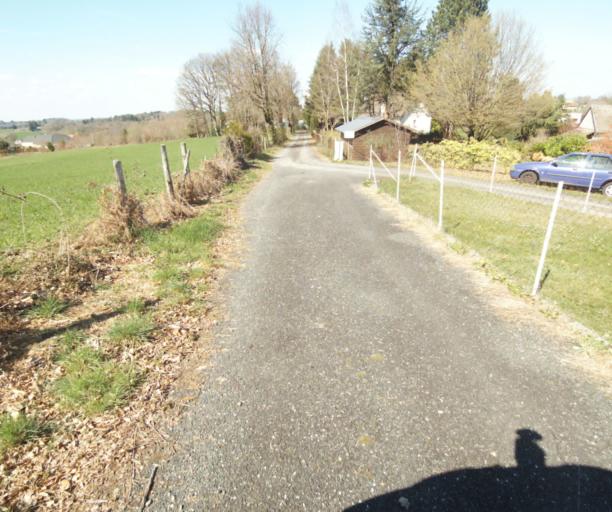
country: FR
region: Limousin
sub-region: Departement de la Correze
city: Saint-Mexant
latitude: 45.2955
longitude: 1.6894
